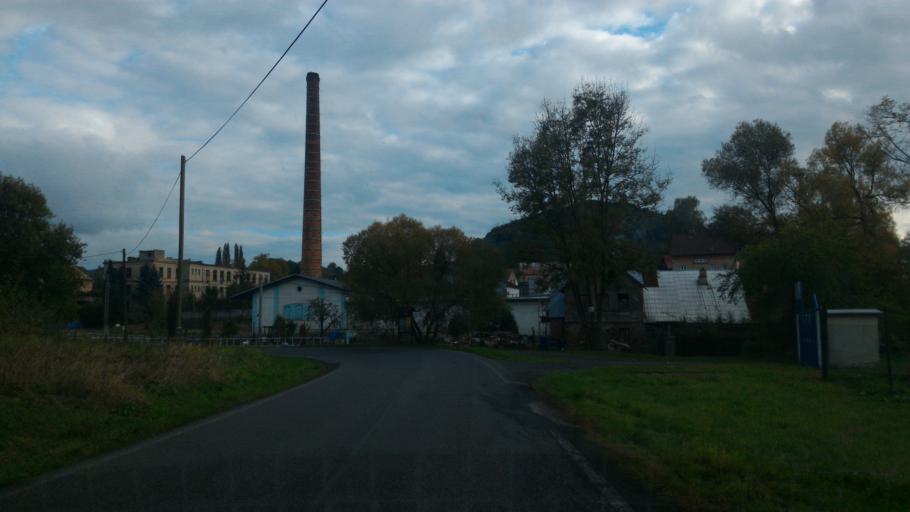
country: CZ
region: Ustecky
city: Ceska Kamenice
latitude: 50.8002
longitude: 14.4055
